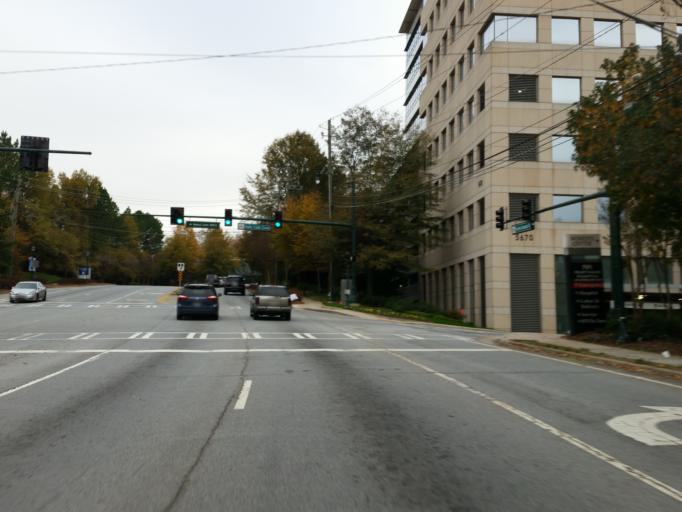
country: US
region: Georgia
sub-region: Fulton County
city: Sandy Springs
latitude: 33.9107
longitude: -84.3530
